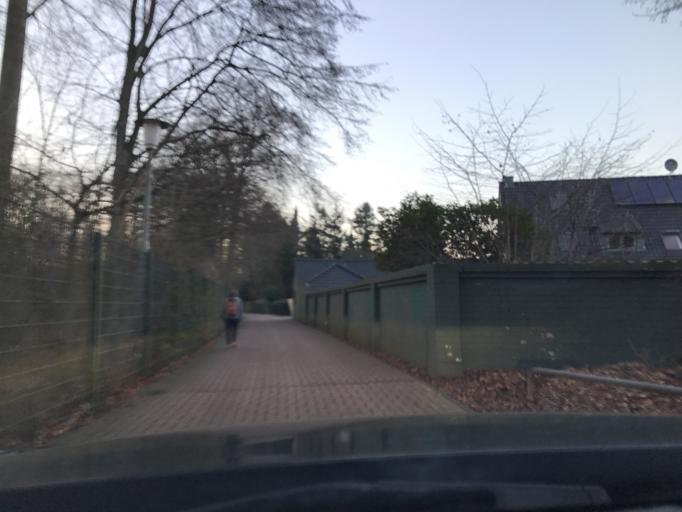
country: DE
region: North Rhine-Westphalia
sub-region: Regierungsbezirk Dusseldorf
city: Krefeld
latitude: 51.3406
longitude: 6.6058
